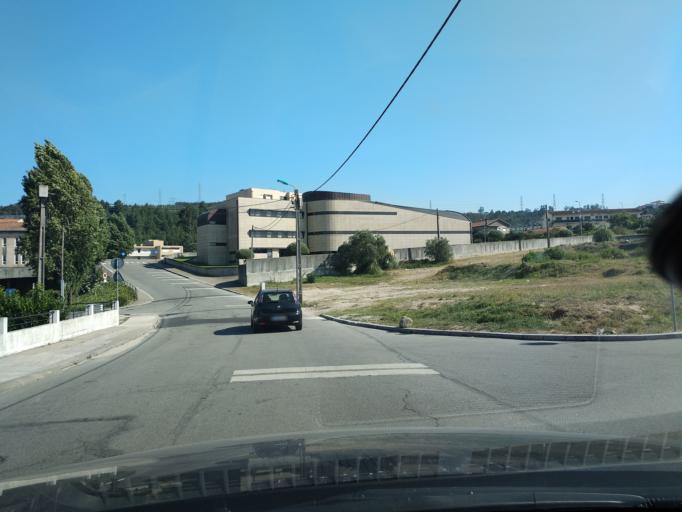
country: PT
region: Porto
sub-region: Paredes
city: Rebordosa
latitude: 41.2209
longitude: -8.4131
